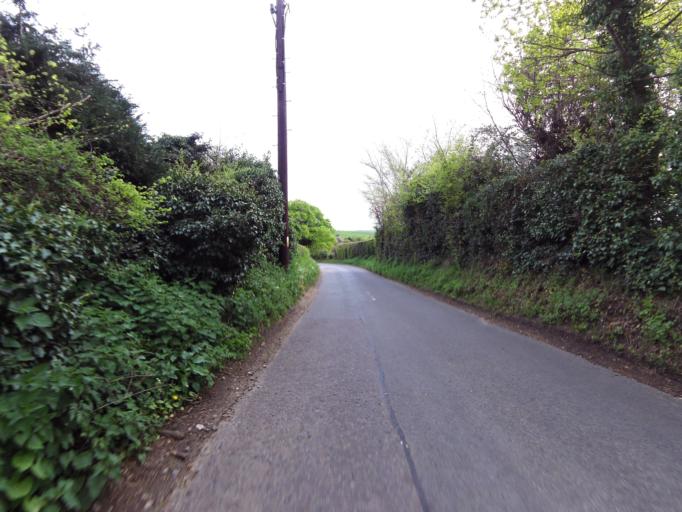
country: GB
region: England
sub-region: Suffolk
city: Ipswich
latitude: 51.9743
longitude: 1.1682
